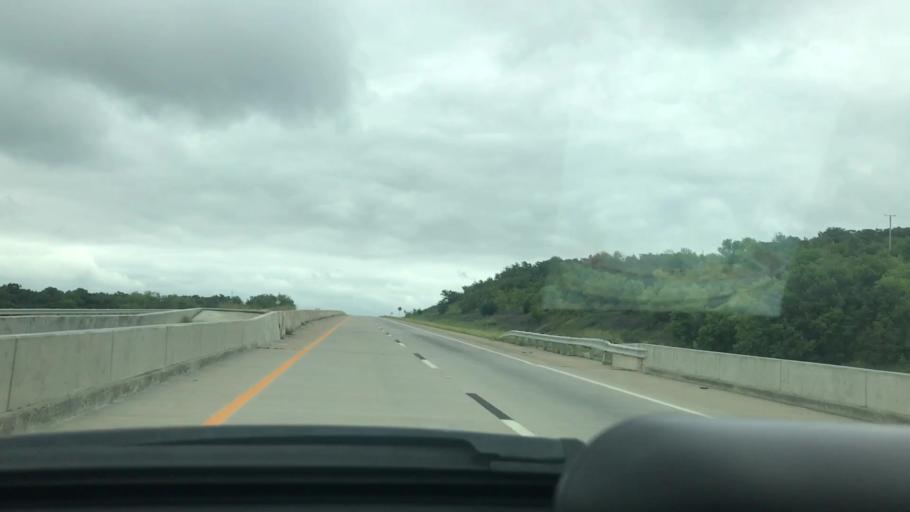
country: US
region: Oklahoma
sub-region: McIntosh County
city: Eufaula
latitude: 35.1720
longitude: -95.6491
